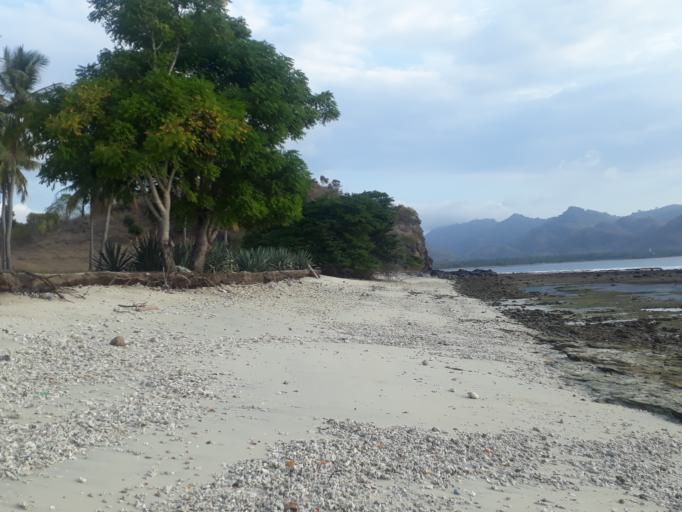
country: ID
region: West Nusa Tenggara
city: Tawun
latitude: -8.7352
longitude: 115.8824
